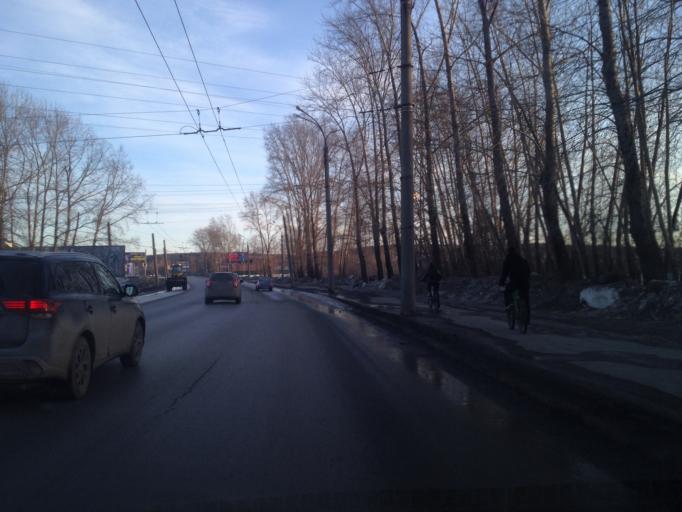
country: RU
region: Sverdlovsk
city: Yekaterinburg
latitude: 56.7589
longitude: 60.6716
